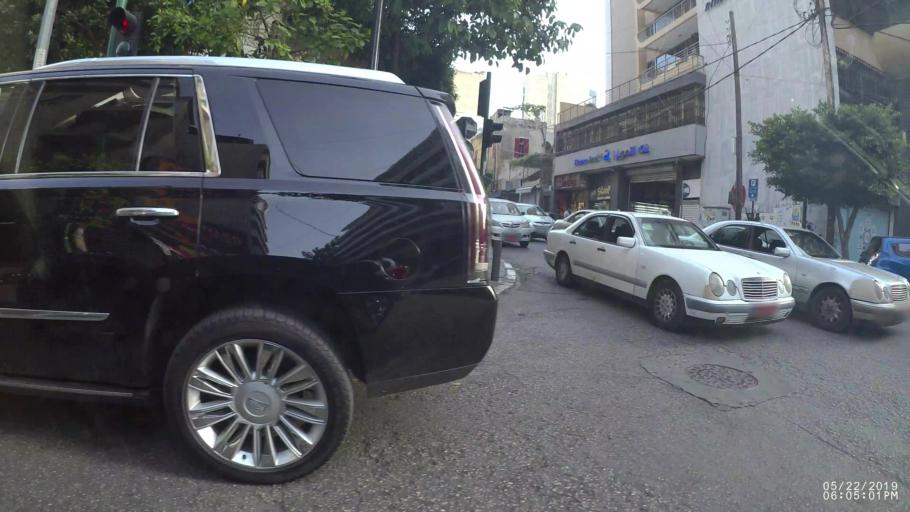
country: LB
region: Beyrouth
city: Ra's Bayrut
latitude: 33.8973
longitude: 35.4838
